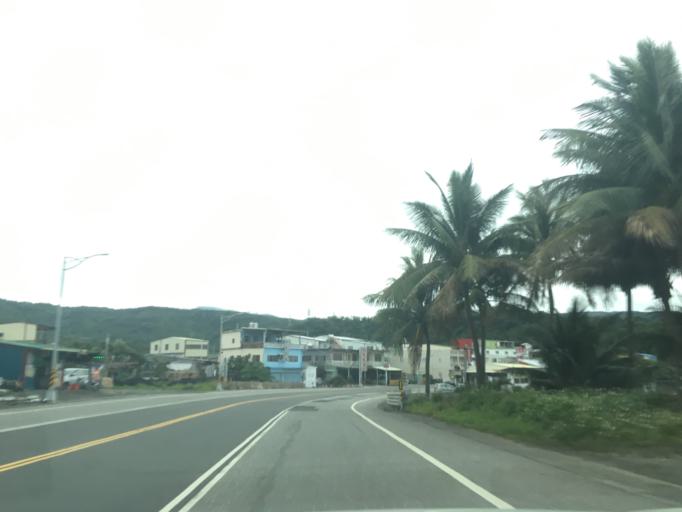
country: TW
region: Taiwan
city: Hengchun
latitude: 22.3380
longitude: 120.8937
